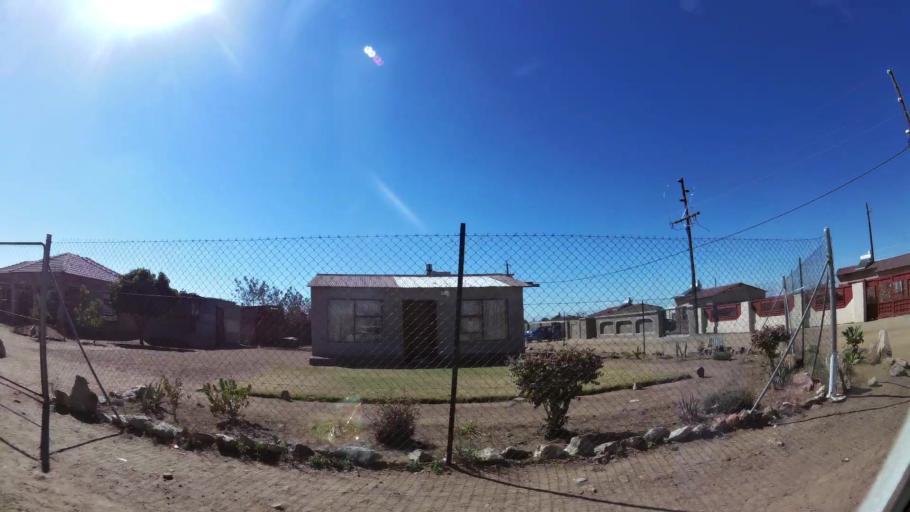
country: ZA
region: Limpopo
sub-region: Capricorn District Municipality
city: Polokwane
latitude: -23.8593
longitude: 29.4146
